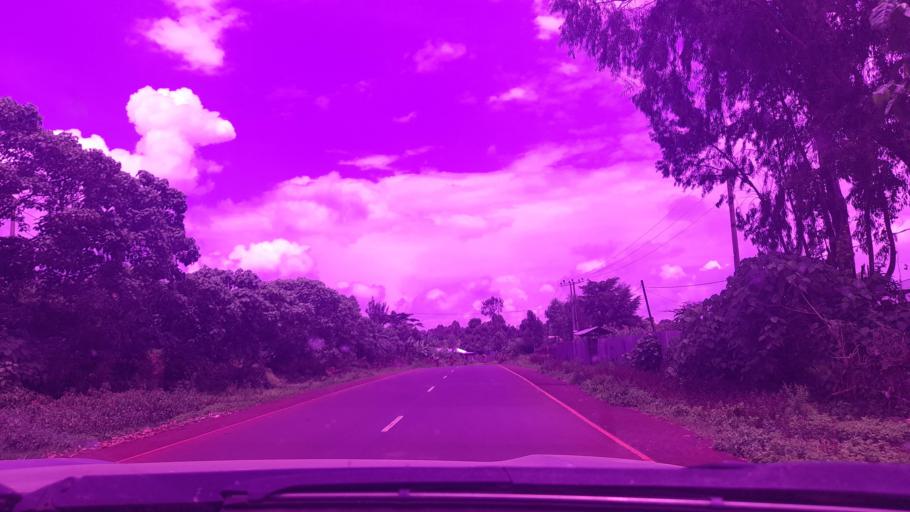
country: ET
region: Oromiya
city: Metu
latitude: 8.3355
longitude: 35.7260
